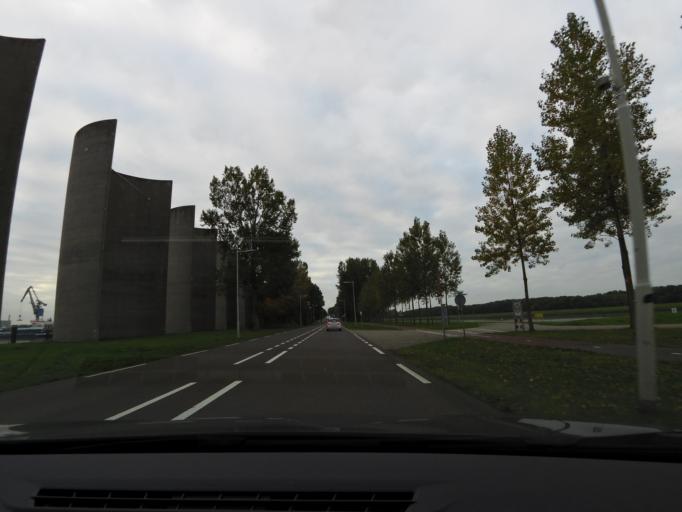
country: NL
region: South Holland
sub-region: Gemeente Maassluis
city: Maassluis
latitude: 51.8971
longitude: 4.2258
